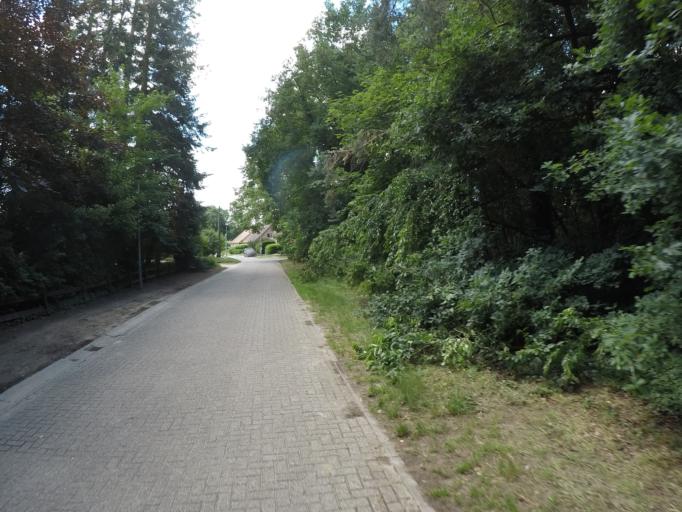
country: BE
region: Flanders
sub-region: Provincie Antwerpen
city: Vosselaar
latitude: 51.3202
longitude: 4.8877
